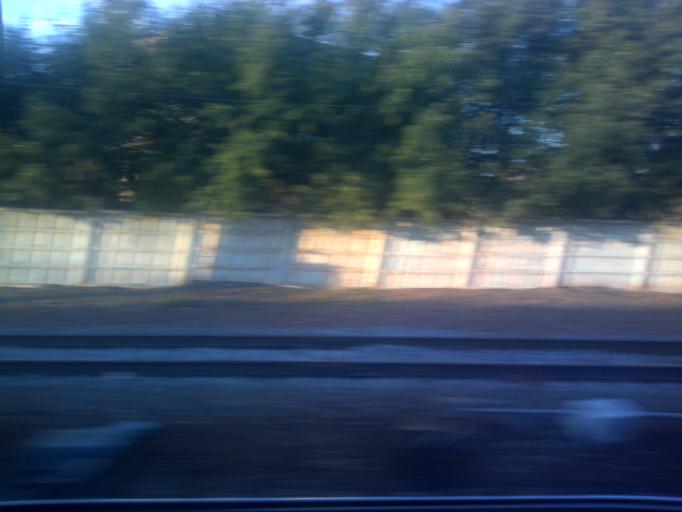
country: RU
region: Moscow
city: Taganskiy
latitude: 55.7479
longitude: 37.6835
